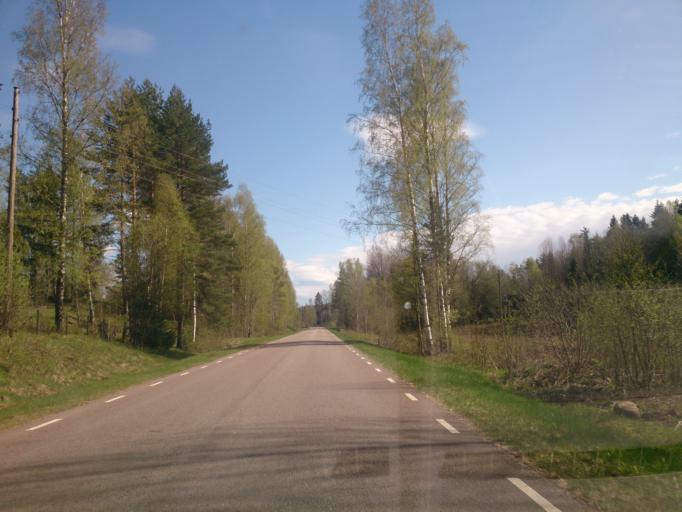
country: SE
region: OEstergoetland
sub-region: Linkopings Kommun
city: Ljungsbro
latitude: 58.6104
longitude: 15.4770
